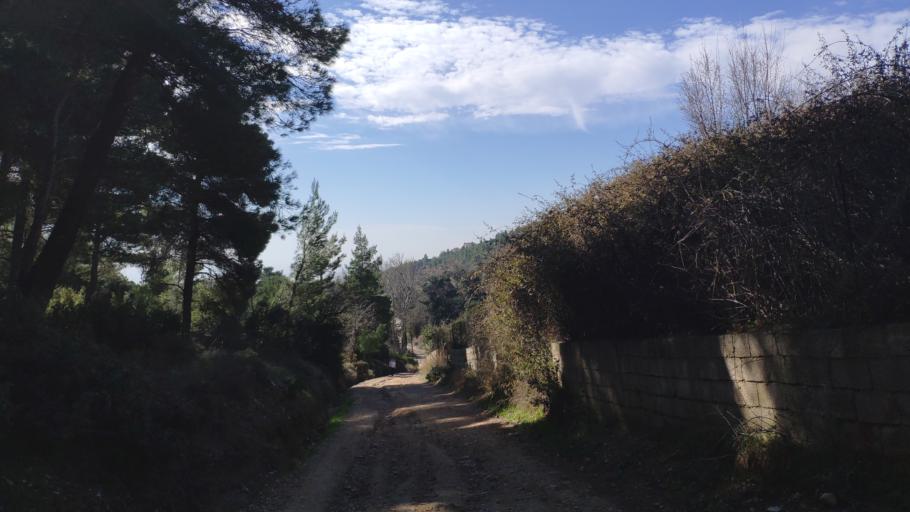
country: GR
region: Attica
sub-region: Nomarchia Anatolikis Attikis
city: Varybobi
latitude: 38.1536
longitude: 23.7766
